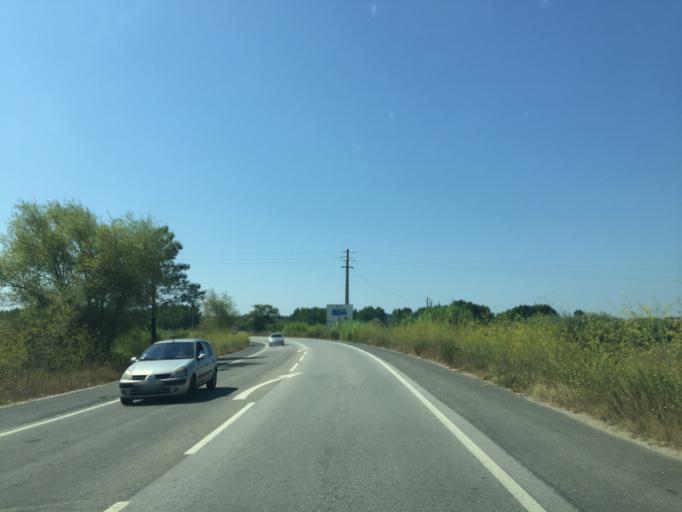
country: PT
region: Aveiro
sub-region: Mealhada
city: Mealhada
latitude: 40.3726
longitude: -8.4711
